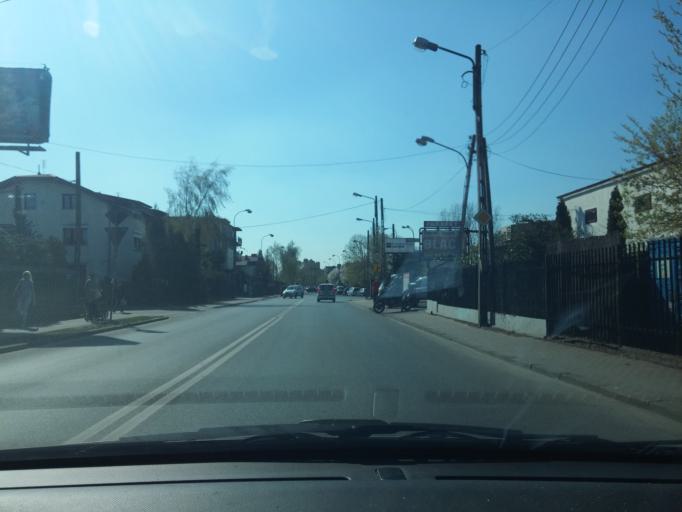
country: PL
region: Masovian Voivodeship
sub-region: Warszawa
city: Rembertow
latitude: 52.2370
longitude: 21.1409
